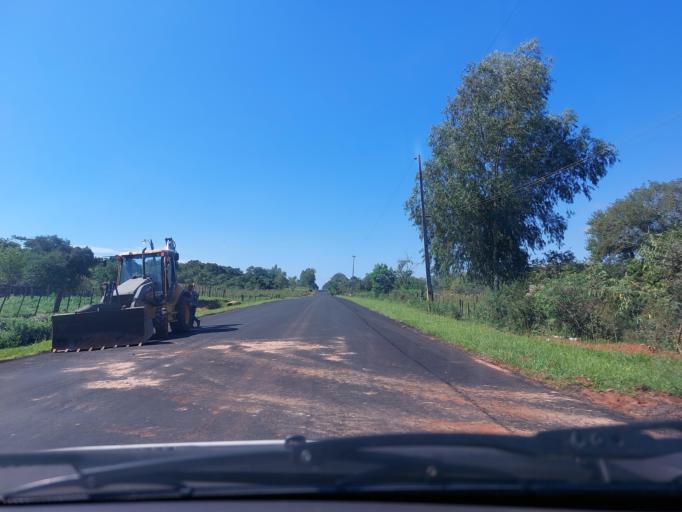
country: PY
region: San Pedro
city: Guayaybi
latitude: -24.5502
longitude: -56.5115
